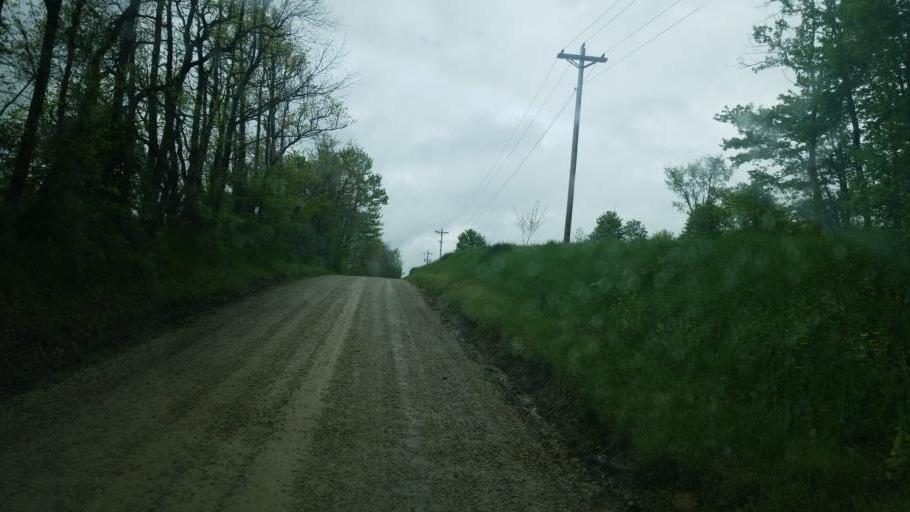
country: US
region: Ohio
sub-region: Tuscarawas County
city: Rockford
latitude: 40.4460
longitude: -81.2464
